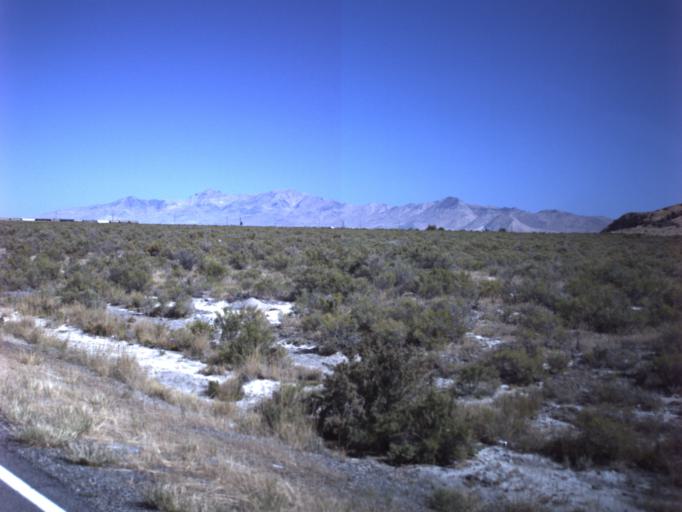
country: US
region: Utah
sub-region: Tooele County
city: Grantsville
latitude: 40.7376
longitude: -112.6554
